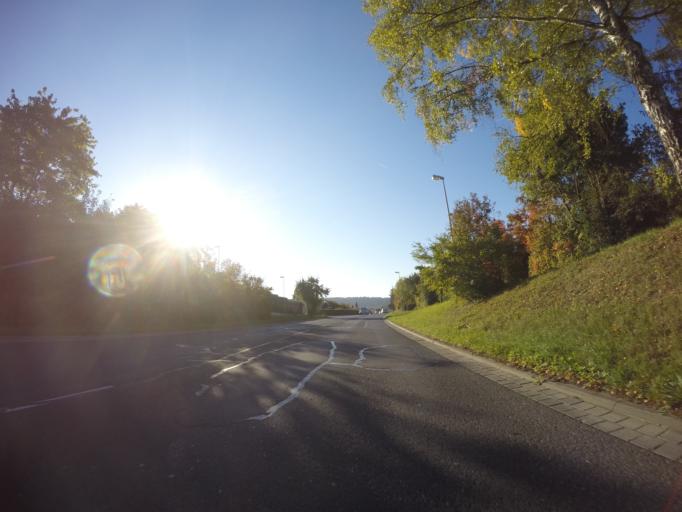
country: DE
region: Bavaria
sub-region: Regierungsbezirk Unterfranken
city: Marktheidenfeld
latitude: 49.8548
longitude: 9.6063
